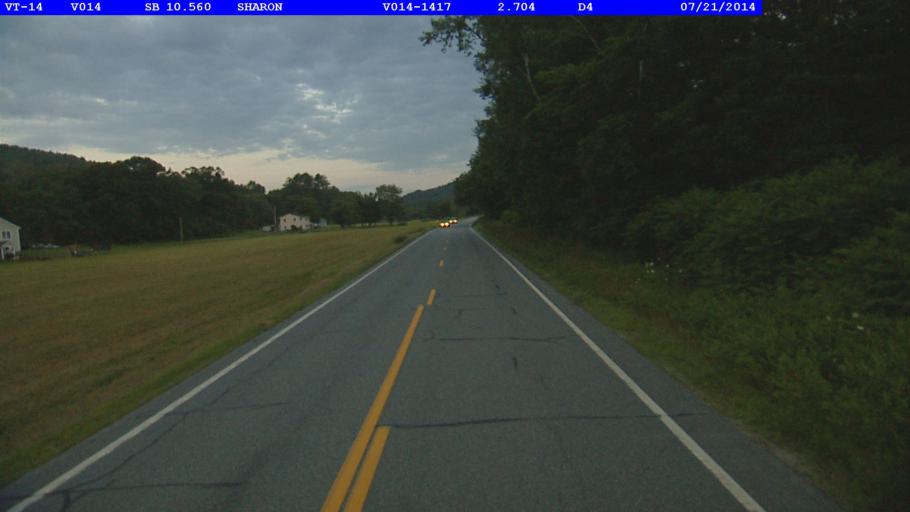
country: US
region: Vermont
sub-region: Windsor County
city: Woodstock
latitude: 43.7554
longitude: -72.4503
